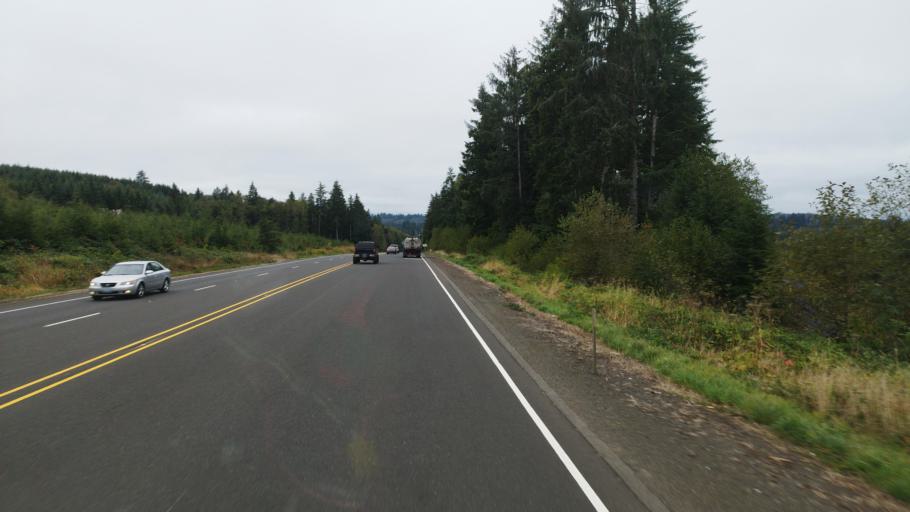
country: US
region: Washington
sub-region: Wahkiakum County
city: Cathlamet
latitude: 46.1718
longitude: -123.5555
